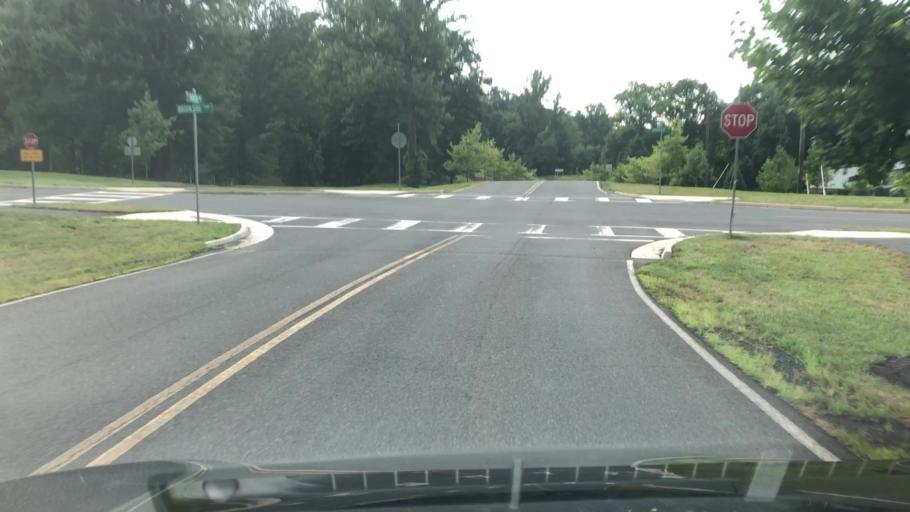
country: US
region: Virginia
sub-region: Fauquier County
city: New Baltimore
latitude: 38.7450
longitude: -77.6865
